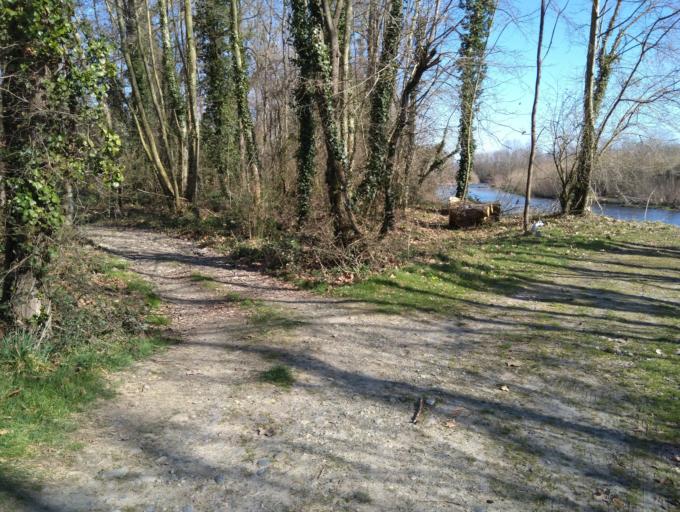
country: FR
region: Midi-Pyrenees
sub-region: Departement des Hautes-Pyrenees
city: Maubourguet
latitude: 43.5053
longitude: 0.0306
